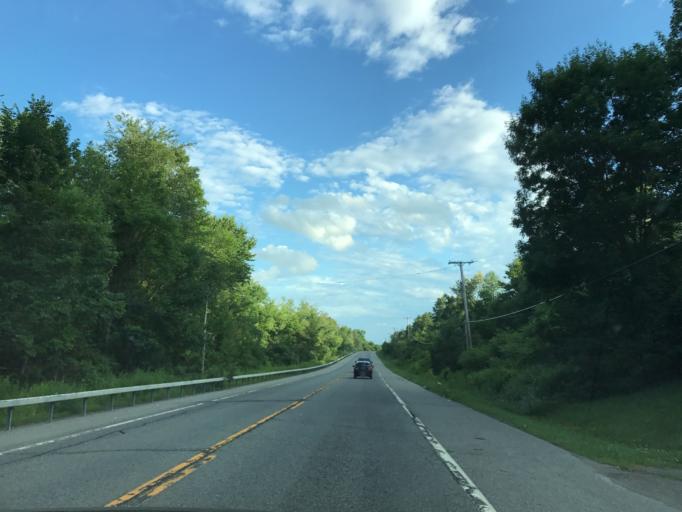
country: US
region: New York
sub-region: Saratoga County
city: Schuylerville
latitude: 43.0819
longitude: -73.5831
